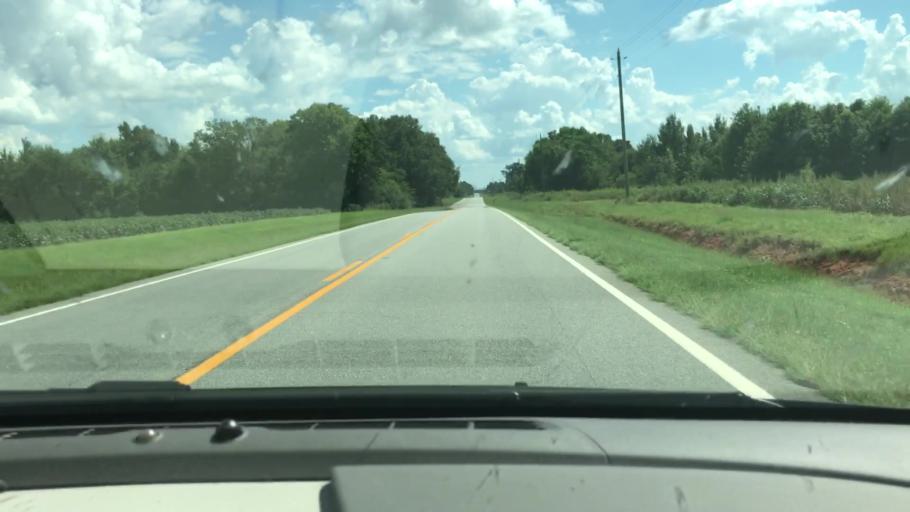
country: US
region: Georgia
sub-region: Quitman County
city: Georgetown
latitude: 31.8025
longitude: -85.0929
